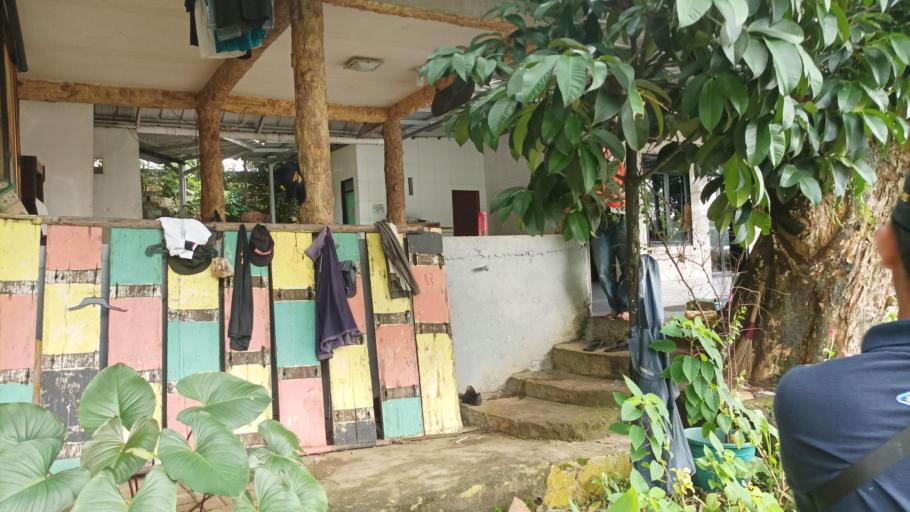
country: ID
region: West Java
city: Depok
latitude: -6.4229
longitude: 106.8584
